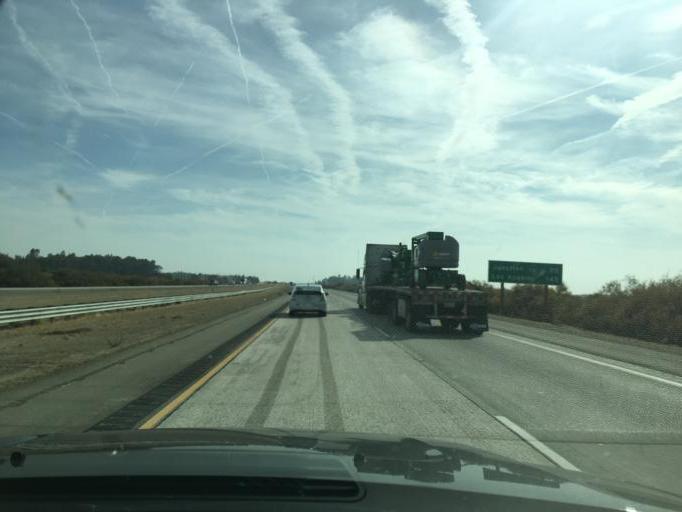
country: US
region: California
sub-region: Kern County
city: Lost Hills
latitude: 35.6066
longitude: -119.6462
